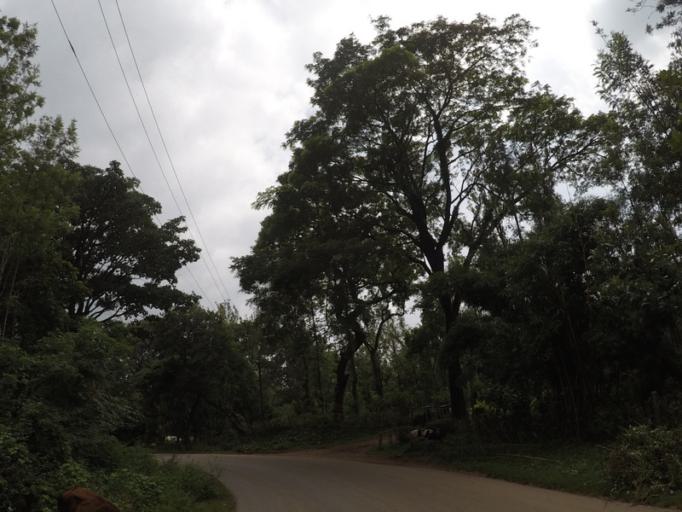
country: IN
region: Karnataka
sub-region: Chikmagalur
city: Chikmagalur
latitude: 13.4520
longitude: 75.8002
